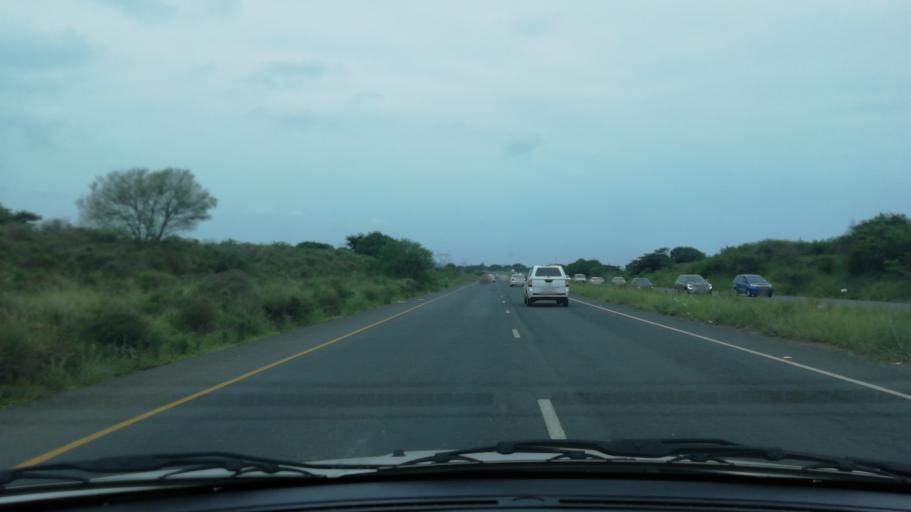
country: ZA
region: KwaZulu-Natal
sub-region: uThungulu District Municipality
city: Richards Bay
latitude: -28.7803
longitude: 31.9932
